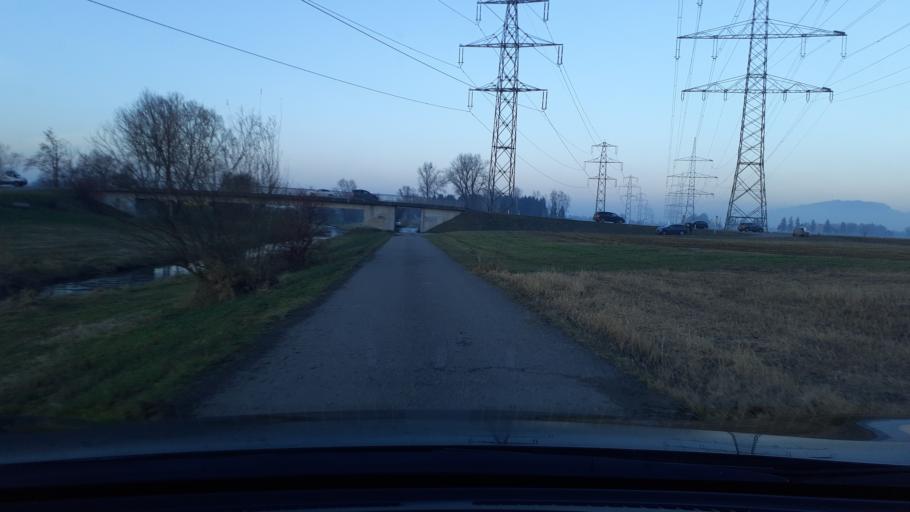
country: AT
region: Vorarlberg
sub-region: Politischer Bezirk Dornbirn
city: Hohenems
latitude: 47.3981
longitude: 9.6855
